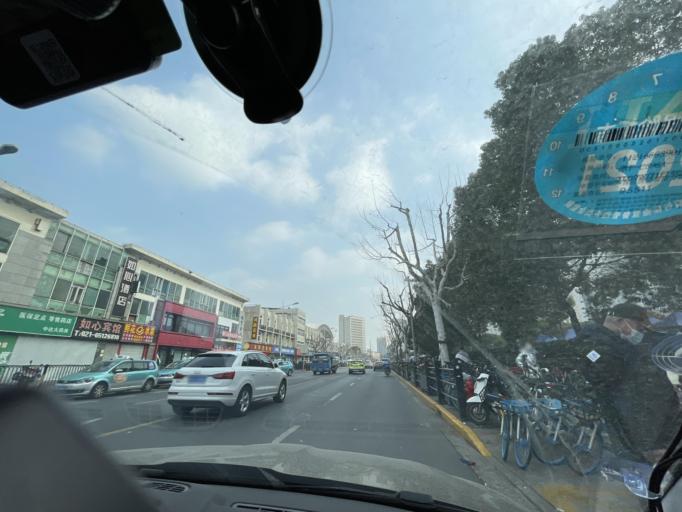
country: CN
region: Shanghai Shi
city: Yangpu
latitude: 31.3116
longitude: 121.5220
